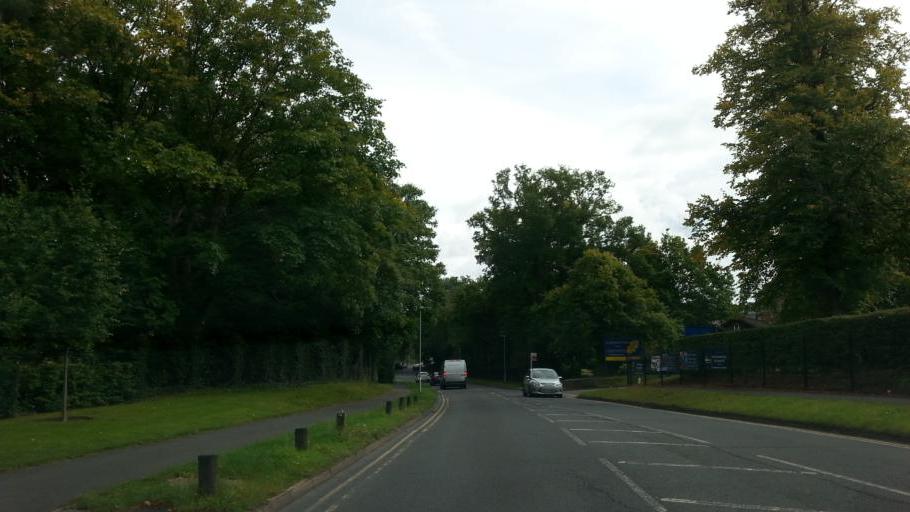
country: GB
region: England
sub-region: Wokingham
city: Earley
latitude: 51.4372
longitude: -0.9455
